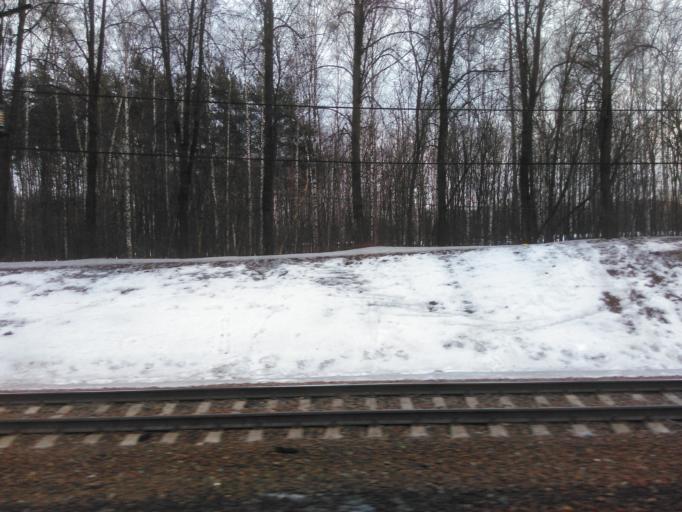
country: RU
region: Moskovskaya
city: Mytishchi
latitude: 55.9254
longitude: 37.7742
